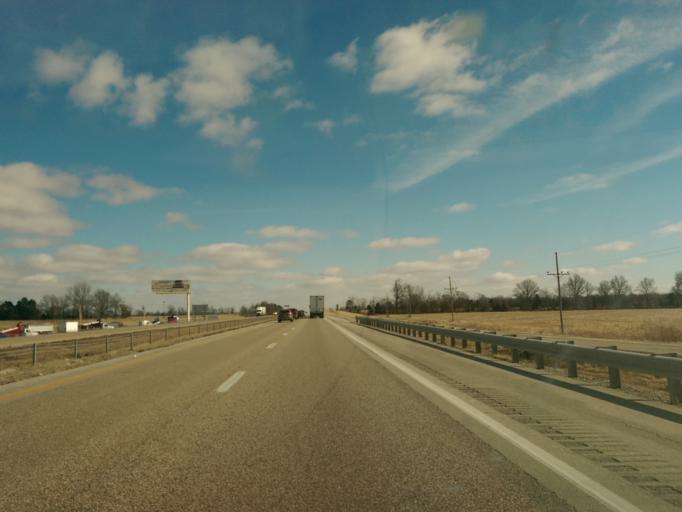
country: US
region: Missouri
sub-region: Montgomery County
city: Montgomery City
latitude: 38.9071
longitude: -91.5229
